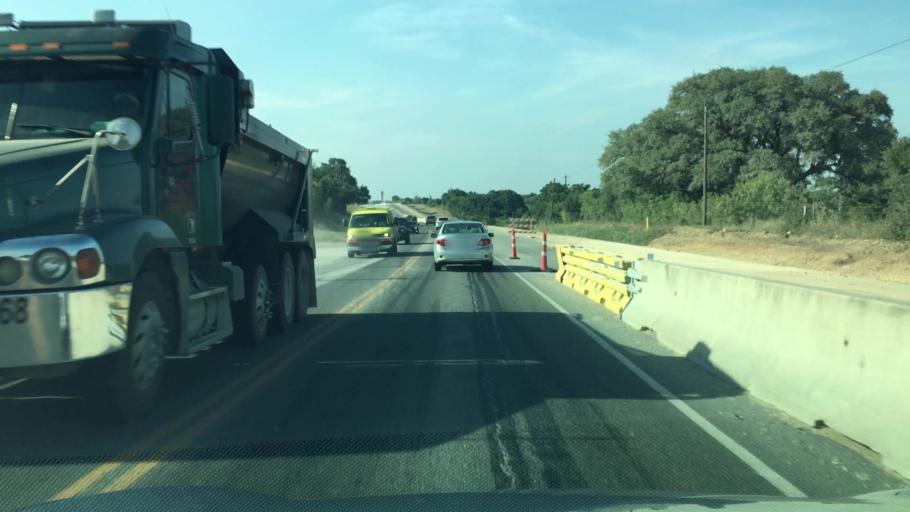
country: US
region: Texas
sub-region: Hays County
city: Buda
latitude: 30.0595
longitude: -97.8739
